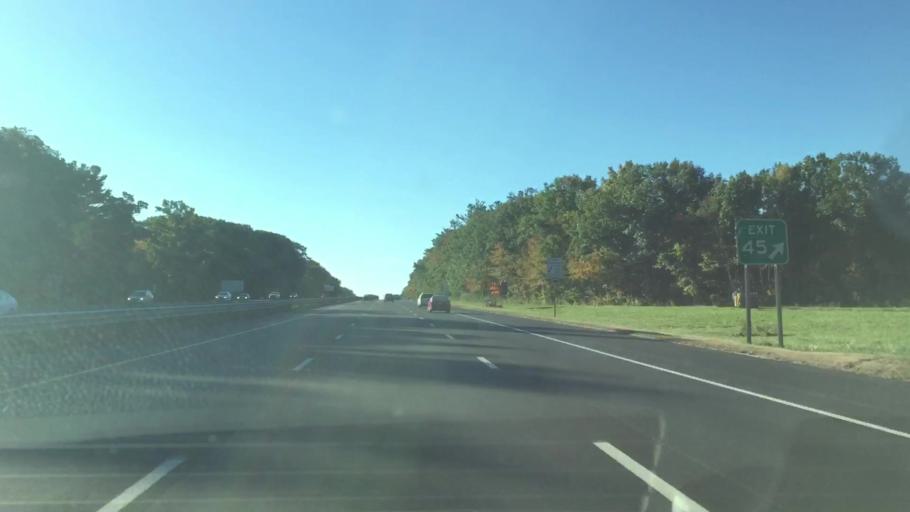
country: US
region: Massachusetts
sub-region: Essex County
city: Methuen
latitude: 42.6893
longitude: -71.2060
